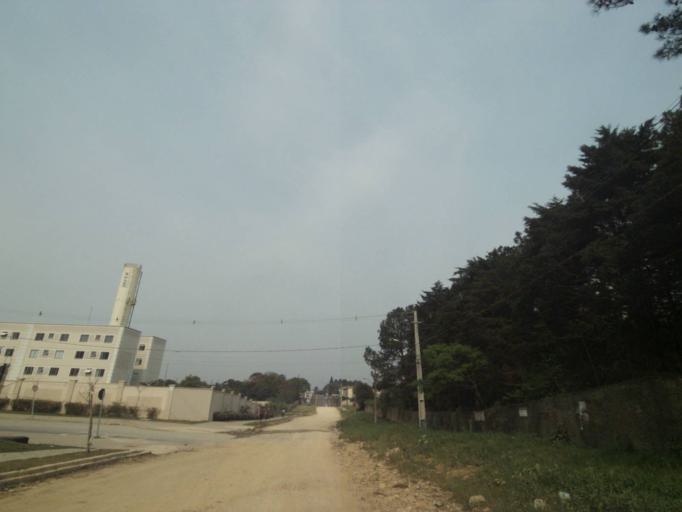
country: BR
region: Parana
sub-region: Sao Jose Dos Pinhais
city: Sao Jose dos Pinhais
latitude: -25.5145
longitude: -49.2857
